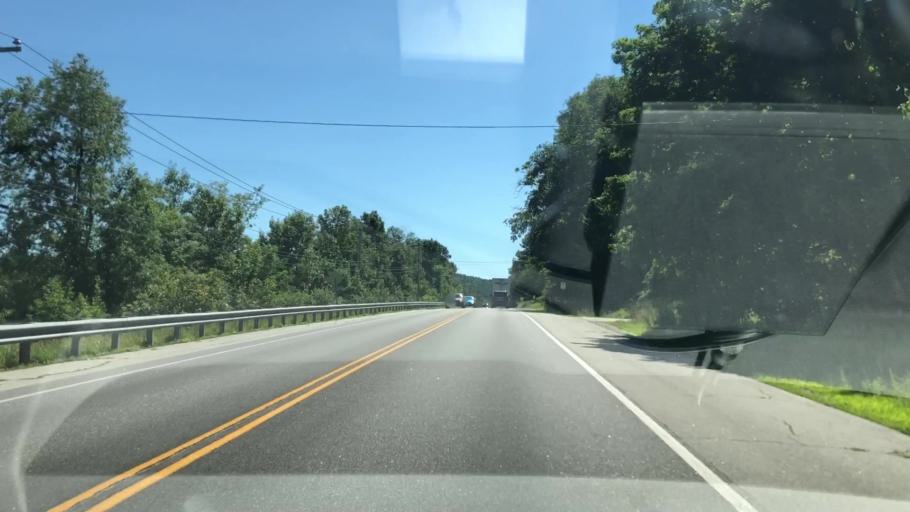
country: US
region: New Hampshire
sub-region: Hillsborough County
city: Bedford
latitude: 42.9040
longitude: -71.5730
